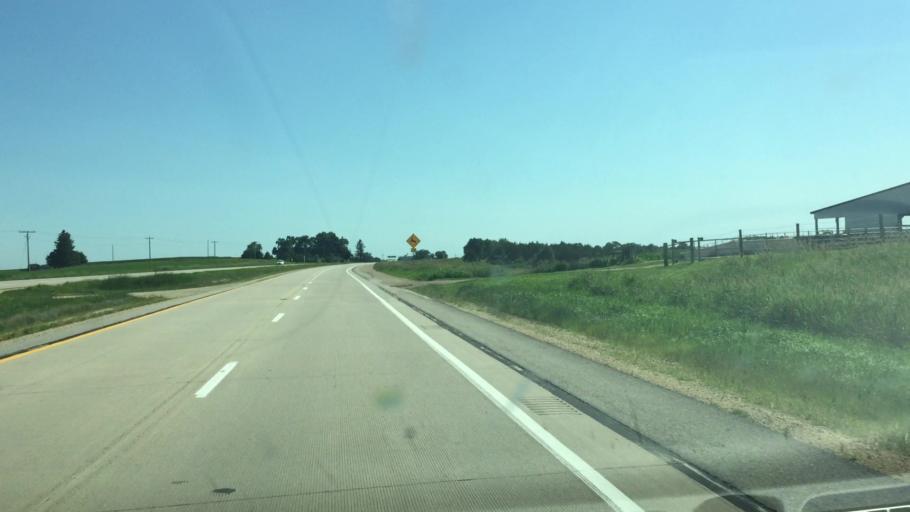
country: US
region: Iowa
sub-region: Jones County
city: Monticello
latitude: 42.2713
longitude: -91.1416
